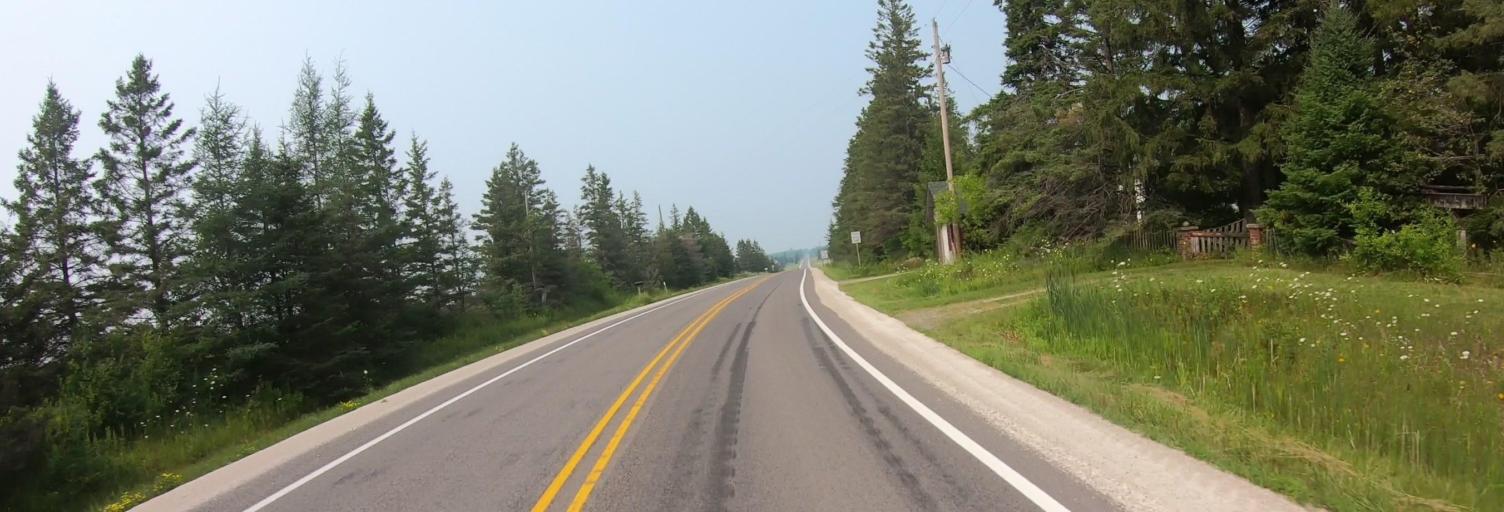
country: US
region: Michigan
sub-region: Chippewa County
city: Sault Ste. Marie
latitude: 46.0736
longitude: -84.2391
